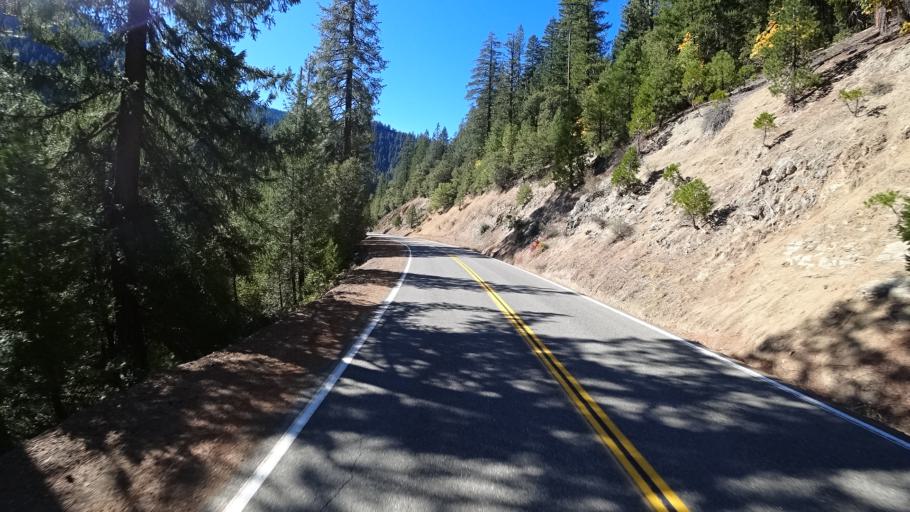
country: US
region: California
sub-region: Trinity County
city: Weaverville
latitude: 41.2230
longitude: -123.0091
